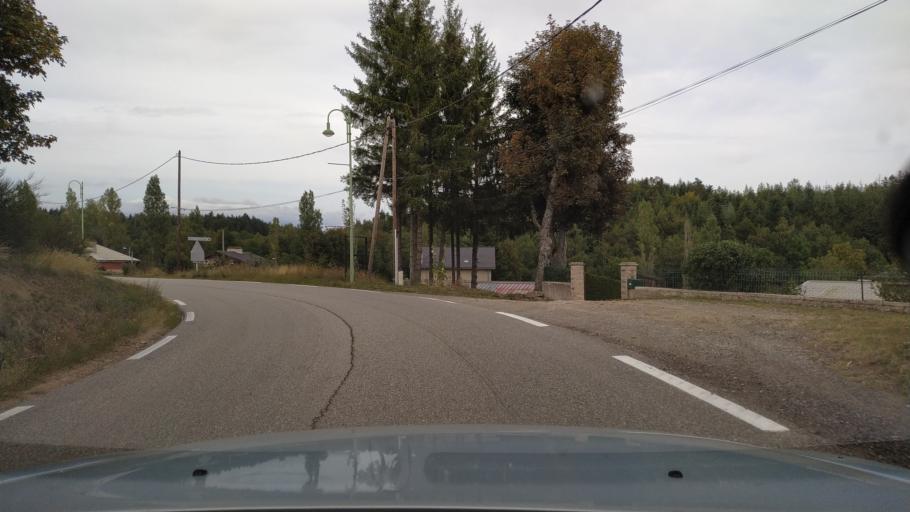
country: FR
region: Rhone-Alpes
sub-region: Departement de l'Ardeche
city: Saint-Agreve
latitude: 45.0129
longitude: 4.4040
